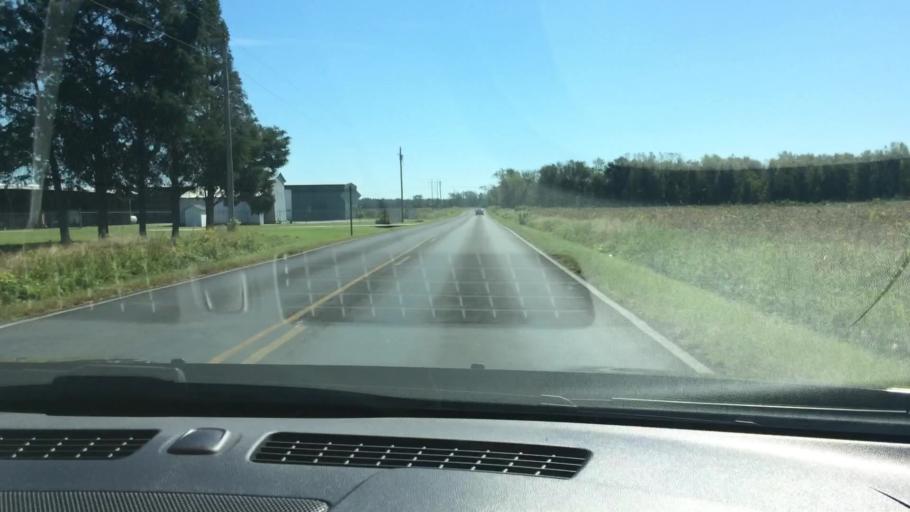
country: US
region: North Carolina
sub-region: Pitt County
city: Grifton
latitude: 35.3735
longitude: -77.3583
